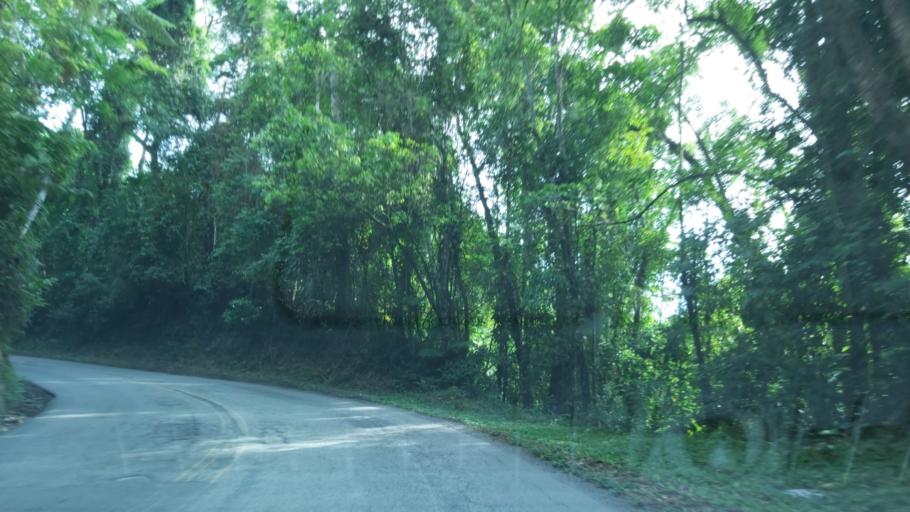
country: BR
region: Sao Paulo
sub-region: Juquia
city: Juquia
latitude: -24.0995
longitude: -47.6202
